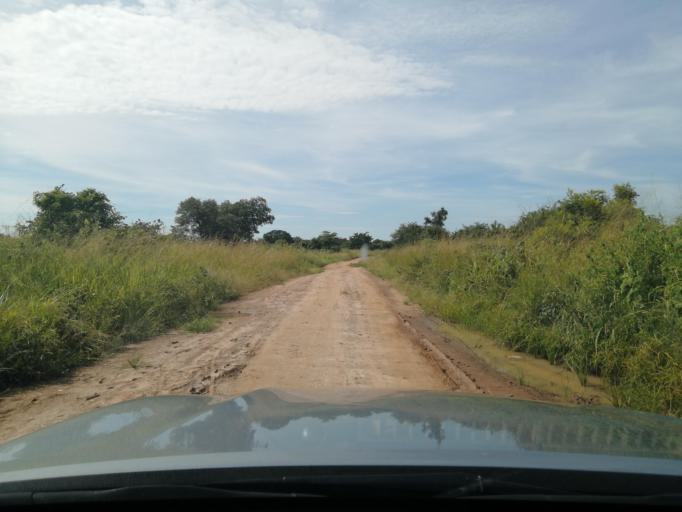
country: ZM
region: Central
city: Chibombo
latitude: -14.9405
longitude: 27.7971
